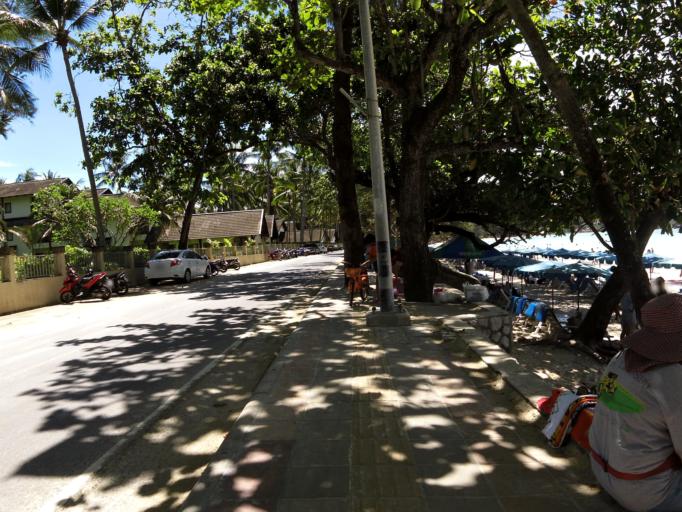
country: TH
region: Phuket
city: Ban Karon
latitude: 7.8237
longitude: 98.2950
